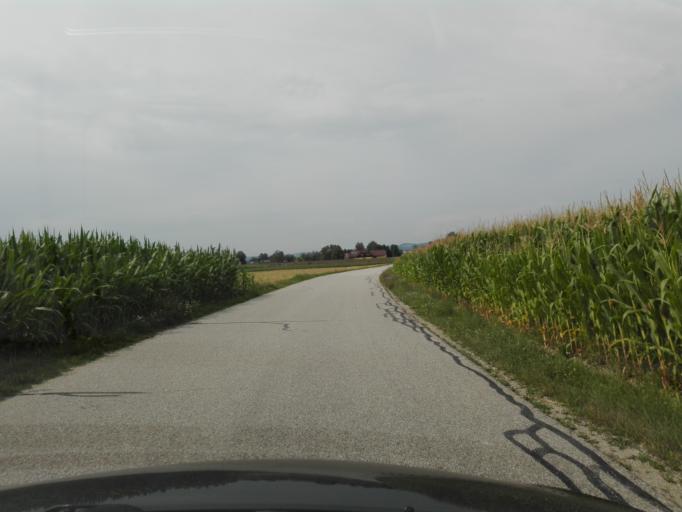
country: AT
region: Lower Austria
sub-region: Politischer Bezirk Amstetten
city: Strengberg
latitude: 48.1816
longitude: 14.6990
